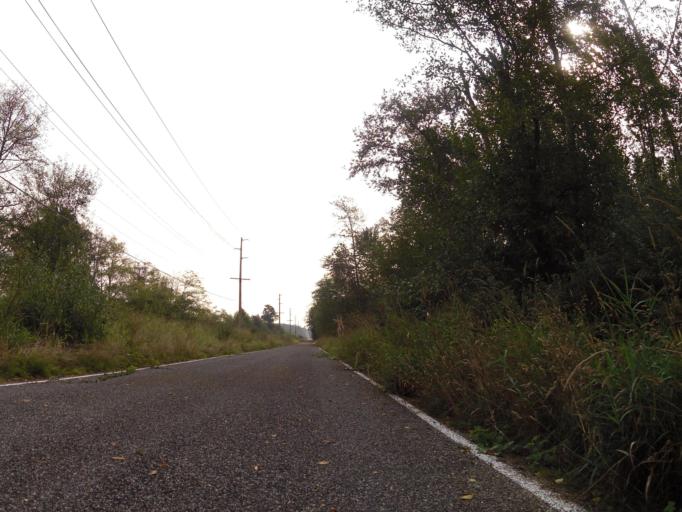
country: US
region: Washington
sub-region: Whatcom County
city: Birch Bay
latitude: 48.8777
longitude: -122.7385
